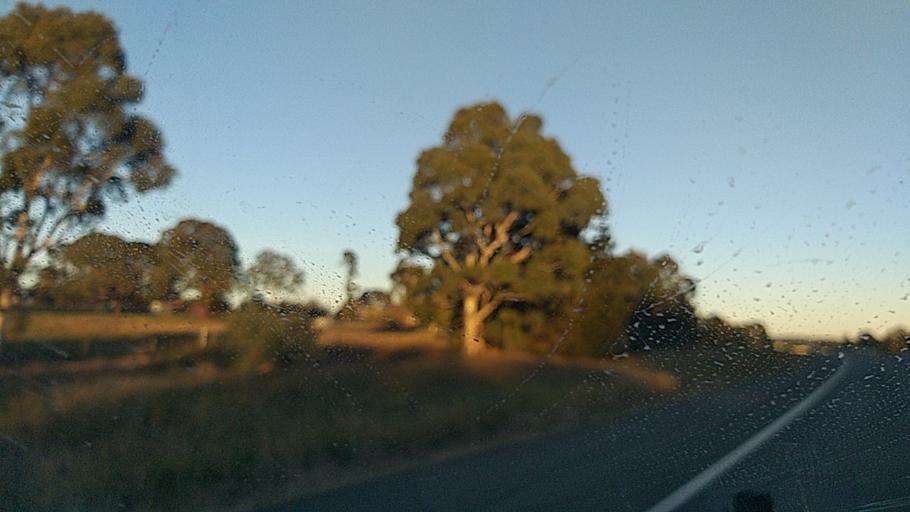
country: AU
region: New South Wales
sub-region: Goulburn Mulwaree
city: Goulburn
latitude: -34.7870
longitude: 149.6349
